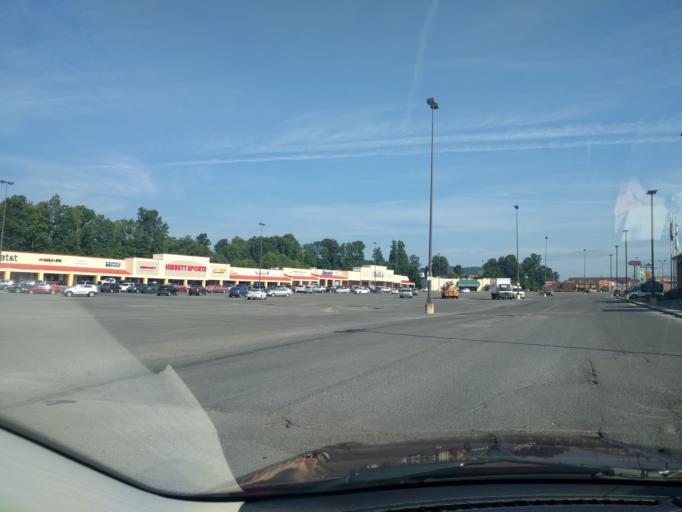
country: US
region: West Virginia
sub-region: Nicholas County
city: Summersville
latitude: 38.2977
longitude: -80.8341
